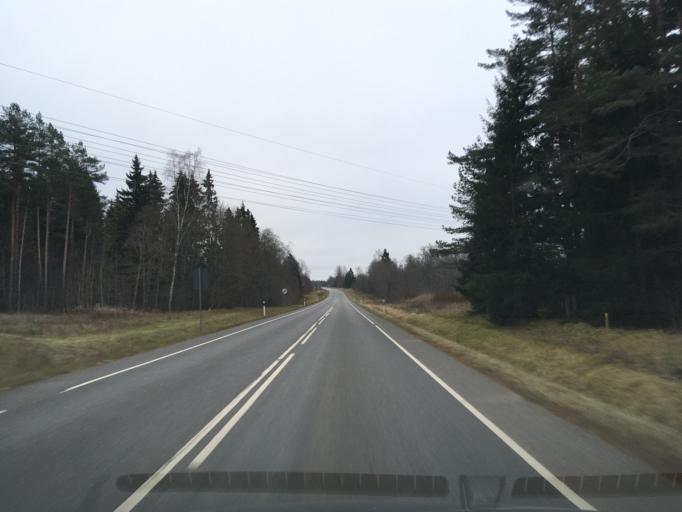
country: EE
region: Laeaene-Virumaa
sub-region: Kadrina vald
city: Kadrina
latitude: 59.4520
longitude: 26.0329
